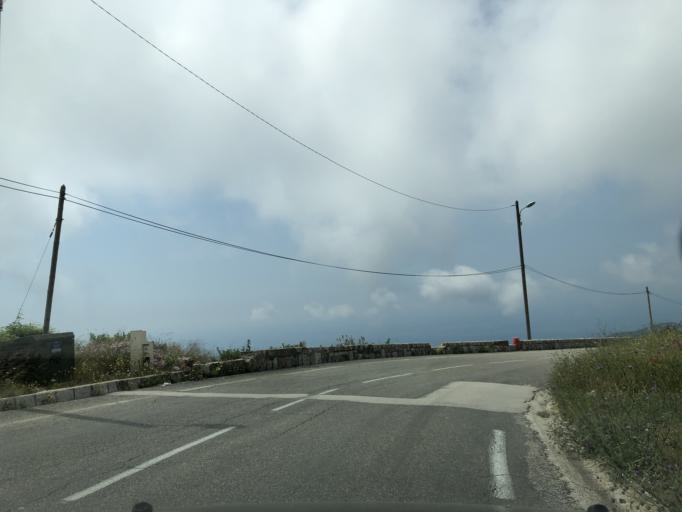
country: FR
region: Provence-Alpes-Cote d'Azur
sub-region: Departement des Alpes-Maritimes
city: Beaulieu-sur-Mer
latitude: 43.7218
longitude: 7.3346
